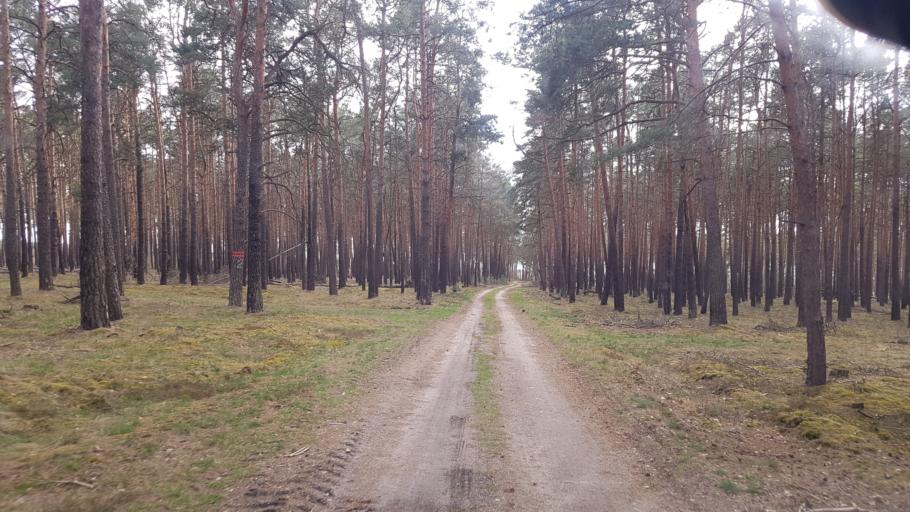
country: DE
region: Brandenburg
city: Schlieben
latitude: 51.6741
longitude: 13.4366
